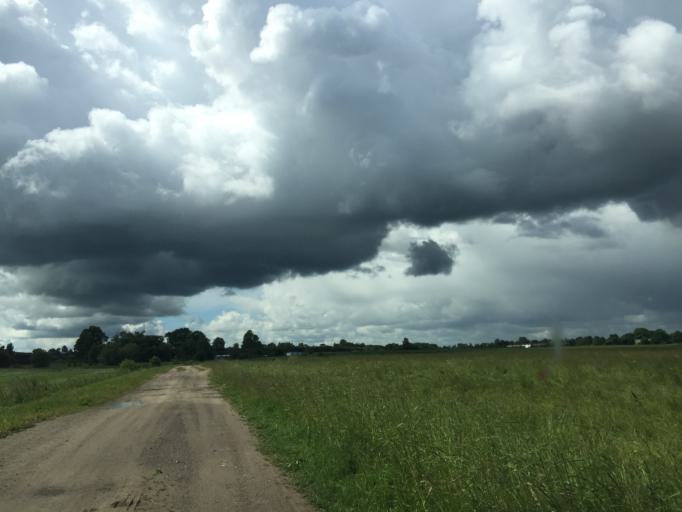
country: LV
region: Lecava
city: Iecava
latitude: 56.6117
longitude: 24.2043
